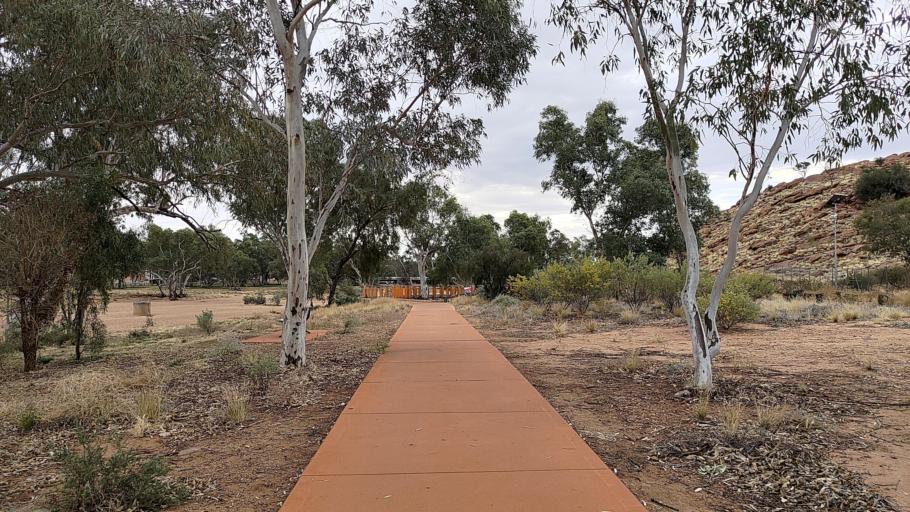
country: AU
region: Northern Territory
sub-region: Alice Springs
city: Alice Springs
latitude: -23.7059
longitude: 133.8828
